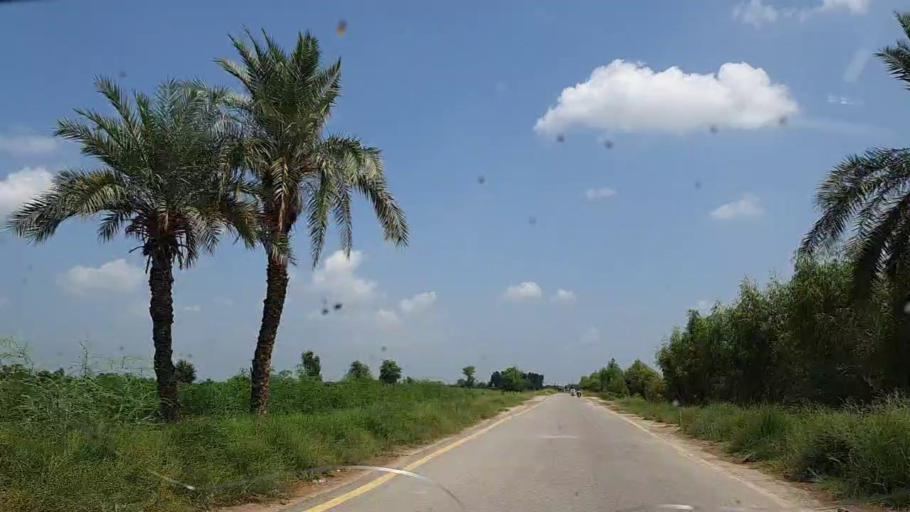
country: PK
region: Sindh
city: Tharu Shah
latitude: 26.9759
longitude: 68.0868
